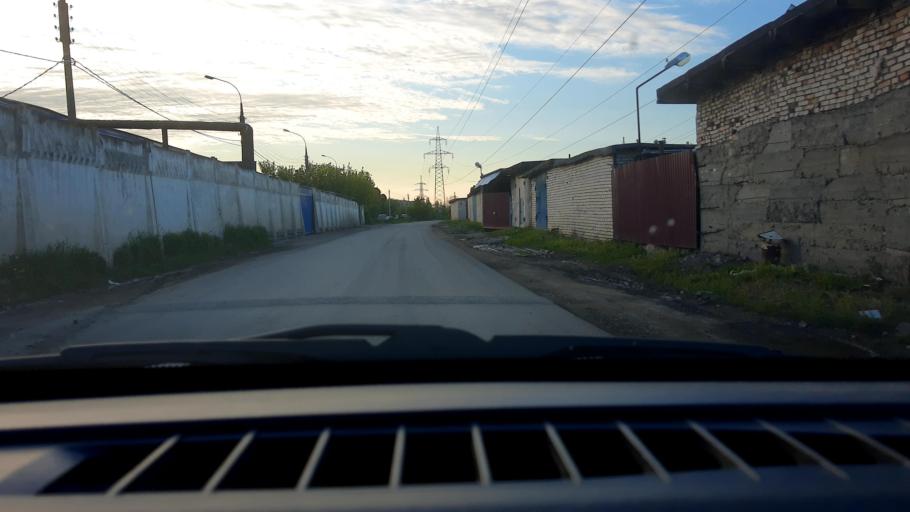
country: RU
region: Nizjnij Novgorod
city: Nizhniy Novgorod
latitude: 56.2756
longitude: 43.8955
